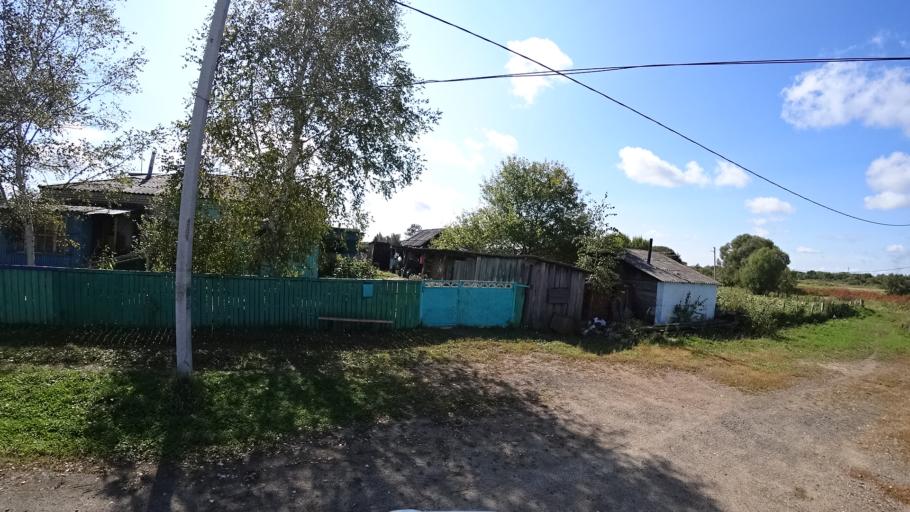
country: RU
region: Amur
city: Arkhara
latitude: 49.4062
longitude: 130.1538
